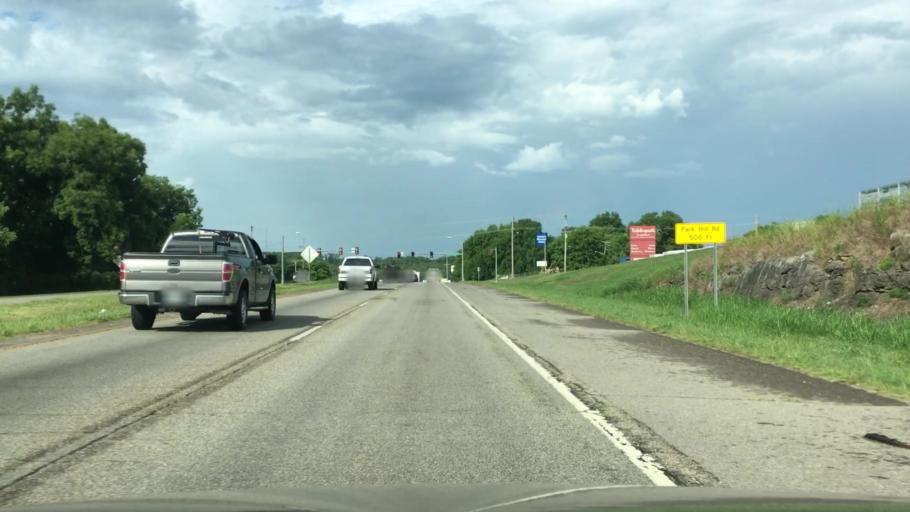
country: US
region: Oklahoma
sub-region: Cherokee County
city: Tahlequah
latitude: 35.8948
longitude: -94.9701
